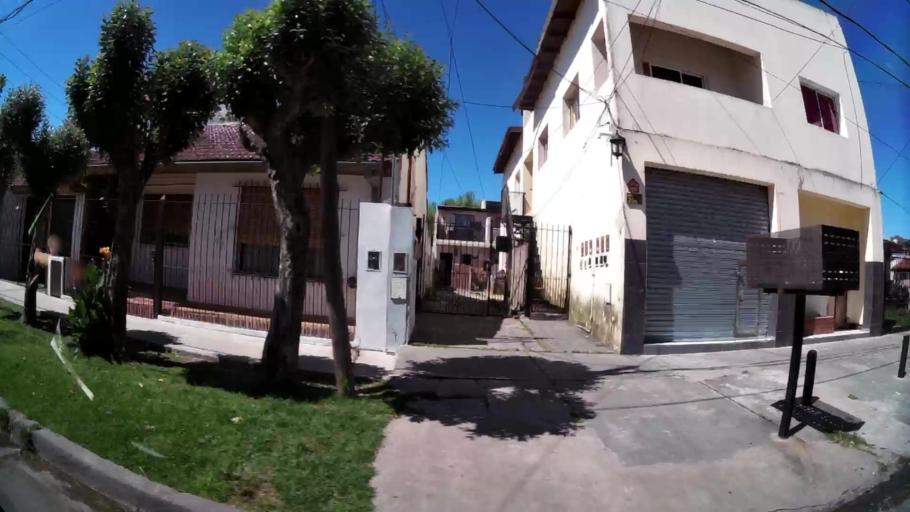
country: AR
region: Buenos Aires
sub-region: Partido de Tigre
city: Tigre
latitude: -34.4945
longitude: -58.6167
